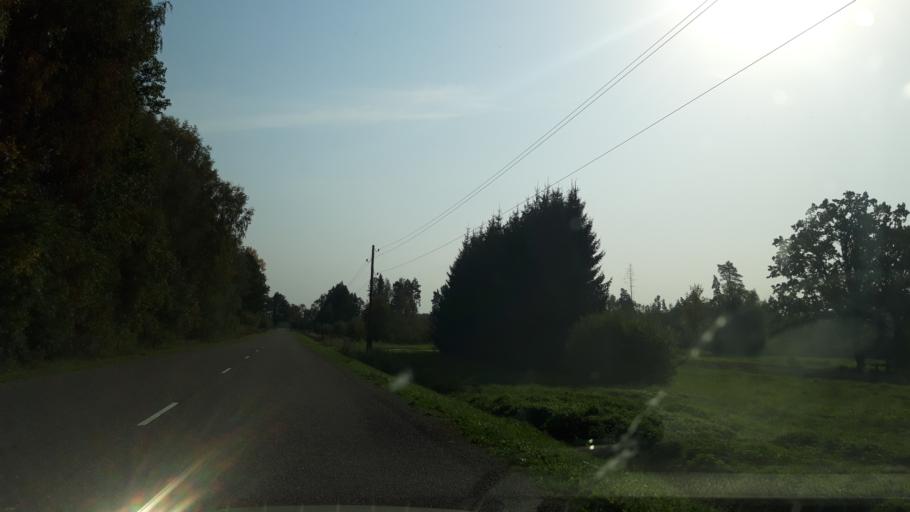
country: LV
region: Burtnieki
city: Matisi
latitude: 57.6302
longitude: 25.2633
